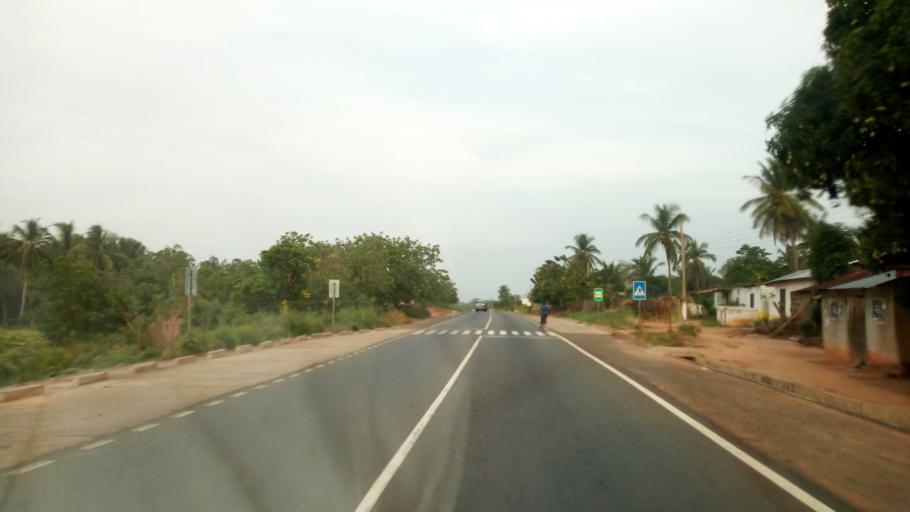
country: TG
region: Maritime
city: Lome
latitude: 6.0964
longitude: 1.0858
